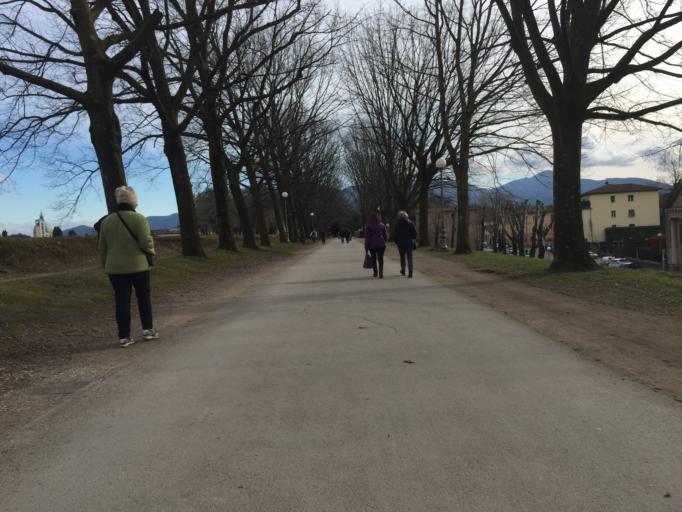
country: IT
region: Tuscany
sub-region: Provincia di Lucca
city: Lucca
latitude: 43.8474
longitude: 10.5141
